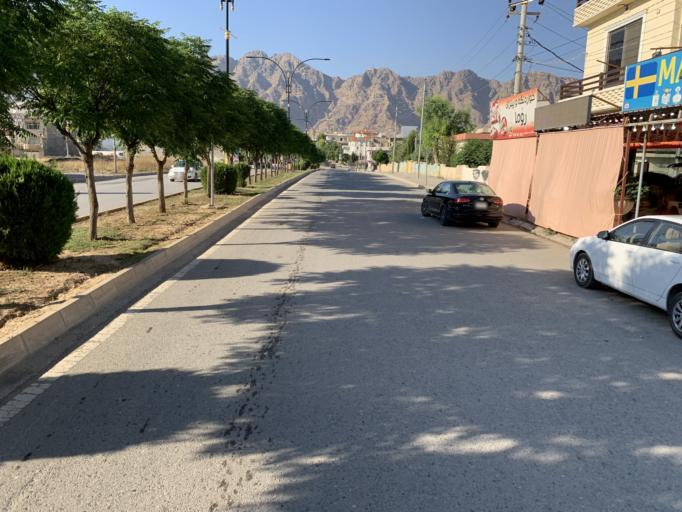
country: IQ
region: As Sulaymaniyah
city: Raniye
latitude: 36.2456
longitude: 44.8743
